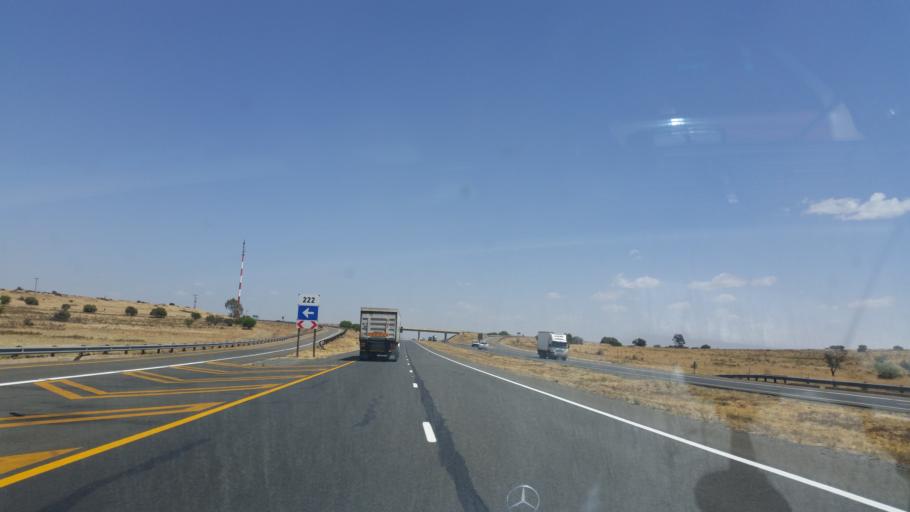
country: ZA
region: Orange Free State
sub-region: Lejweleputswa District Municipality
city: Brandfort
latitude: -28.9314
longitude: 26.4249
